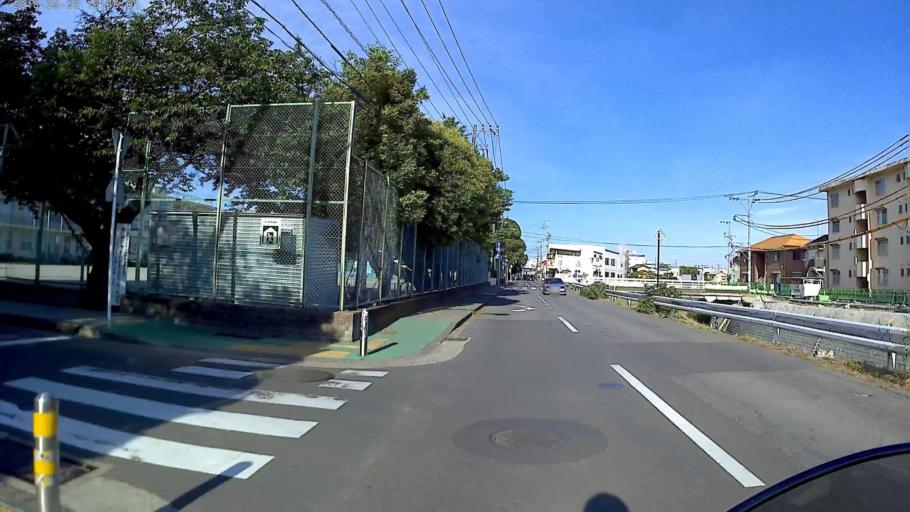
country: JP
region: Kanagawa
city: Odawara
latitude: 35.2685
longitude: 139.1561
